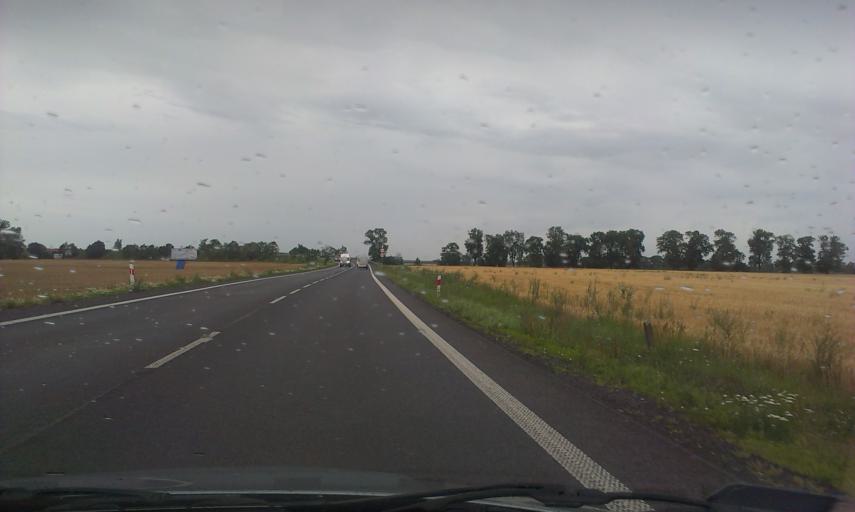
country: PL
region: Greater Poland Voivodeship
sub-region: Powiat obornicki
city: Oborniki
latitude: 52.5979
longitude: 16.8237
